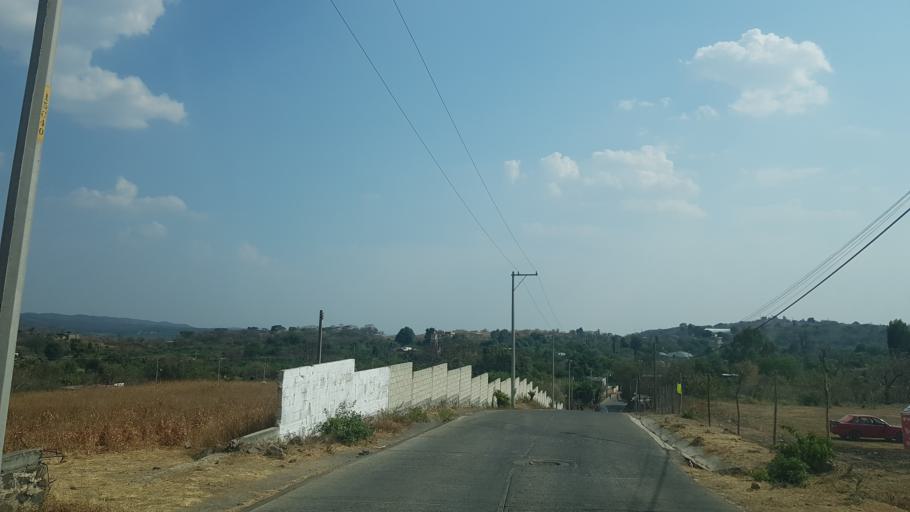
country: MX
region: Puebla
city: San Juan Amecac
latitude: 18.8244
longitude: -98.7042
